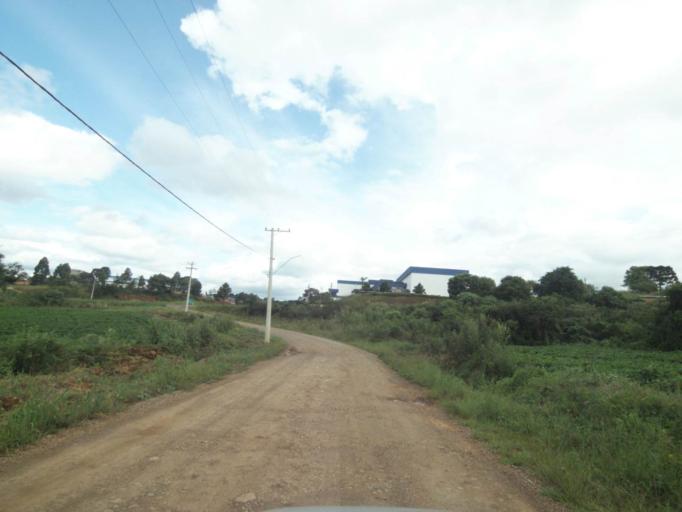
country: BR
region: Rio Grande do Sul
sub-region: Lagoa Vermelha
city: Lagoa Vermelha
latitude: -28.2058
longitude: -51.5385
